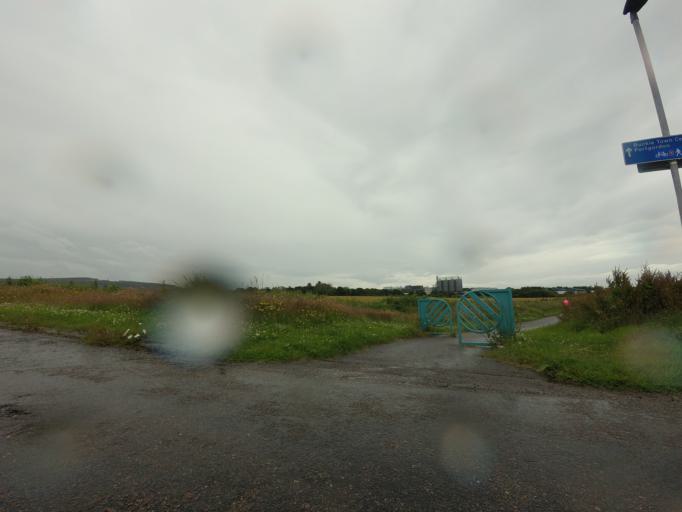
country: GB
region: Scotland
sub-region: Moray
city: Buckie
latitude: 57.6821
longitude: -2.9404
